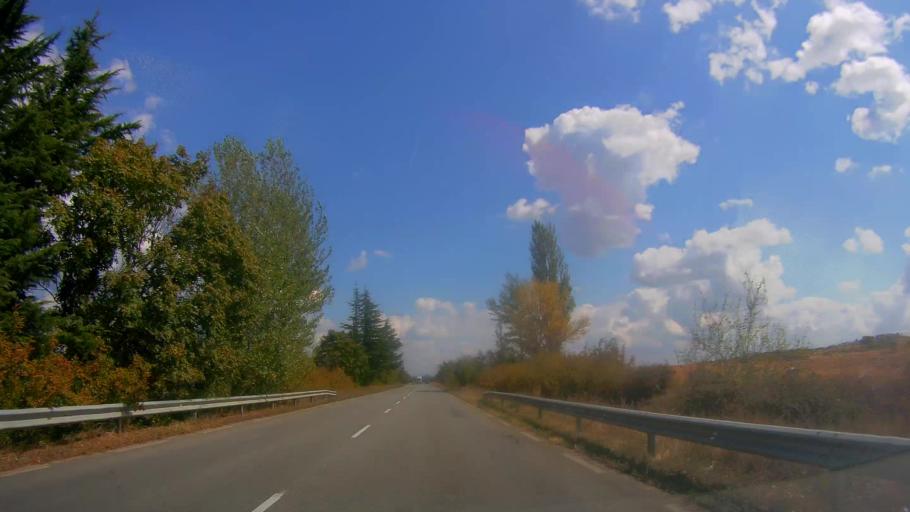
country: BG
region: Sliven
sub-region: Obshtina Tvurditsa
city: Tvurditsa
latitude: 42.6553
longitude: 25.9369
